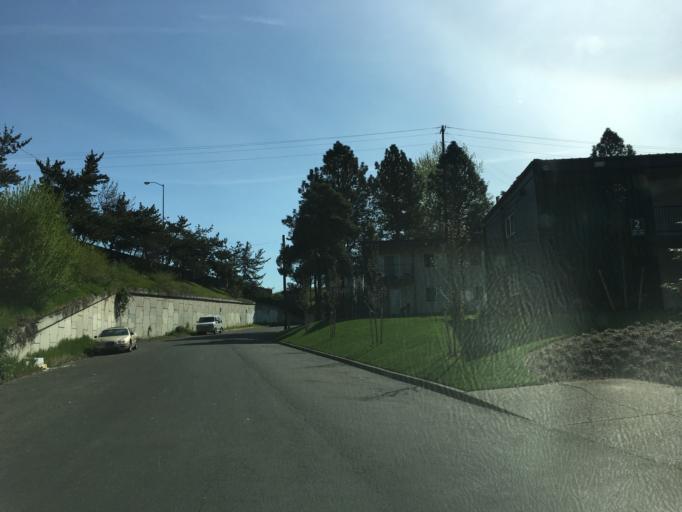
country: US
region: Oregon
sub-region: Multnomah County
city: Lents
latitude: 45.5309
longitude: -122.5697
